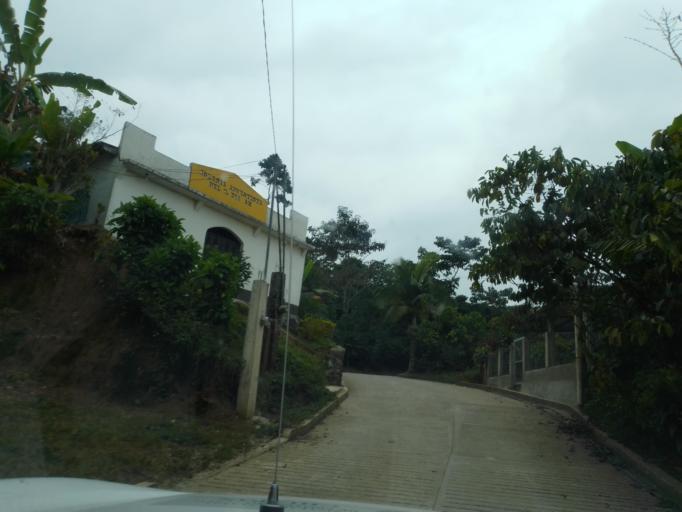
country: MX
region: Chiapas
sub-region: Union Juarez
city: Santo Domingo
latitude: 15.0524
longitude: -92.1145
